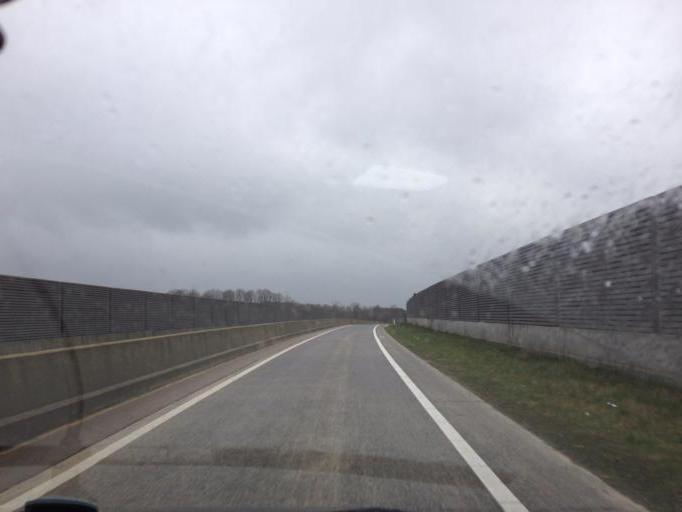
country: BE
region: Flanders
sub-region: Provincie Limburg
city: Opglabbeek
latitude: 51.0950
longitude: 5.5398
